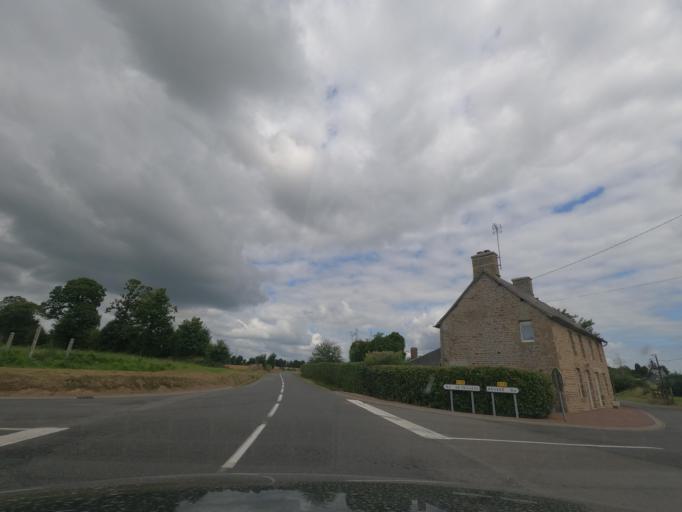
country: FR
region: Lower Normandy
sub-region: Departement de la Manche
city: Le Teilleul
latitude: 48.5074
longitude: -0.9063
